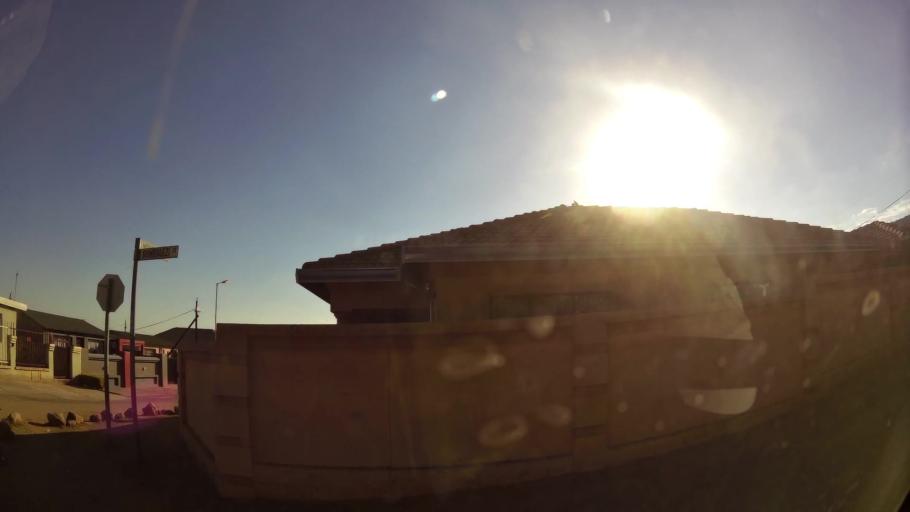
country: ZA
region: Gauteng
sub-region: City of Tshwane Metropolitan Municipality
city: Cullinan
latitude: -25.7069
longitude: 28.3722
